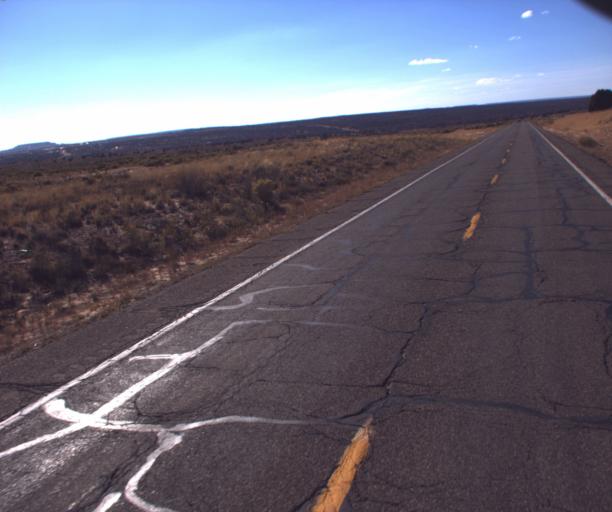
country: US
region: Arizona
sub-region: Coconino County
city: Kaibito
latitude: 36.6130
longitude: -111.0525
